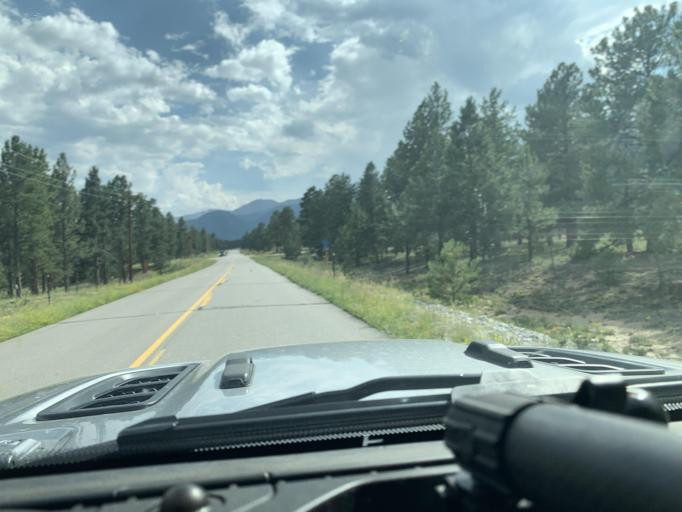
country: US
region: Colorado
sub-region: Chaffee County
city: Buena Vista
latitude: 38.7535
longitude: -106.1552
